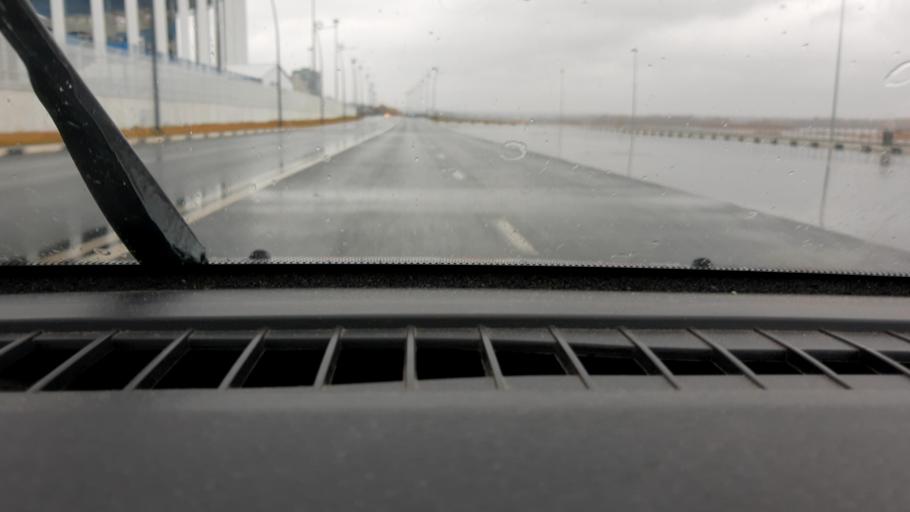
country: RU
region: Nizjnij Novgorod
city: Nizhniy Novgorod
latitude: 56.3373
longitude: 43.9676
